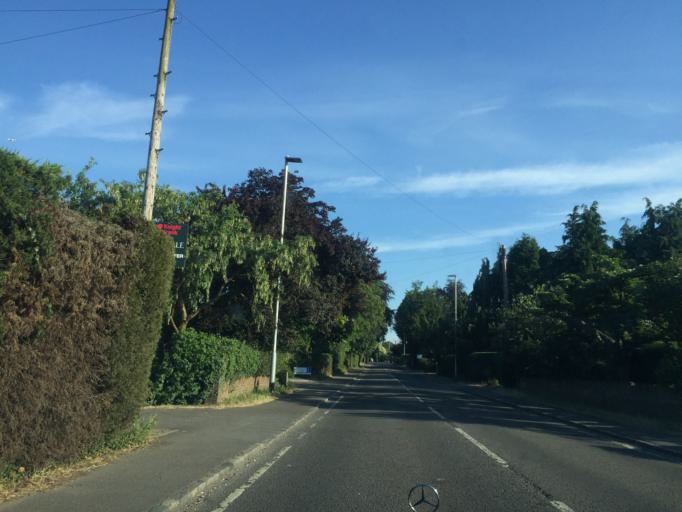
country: GB
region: England
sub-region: Wokingham
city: Twyford
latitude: 51.4821
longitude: -0.8691
